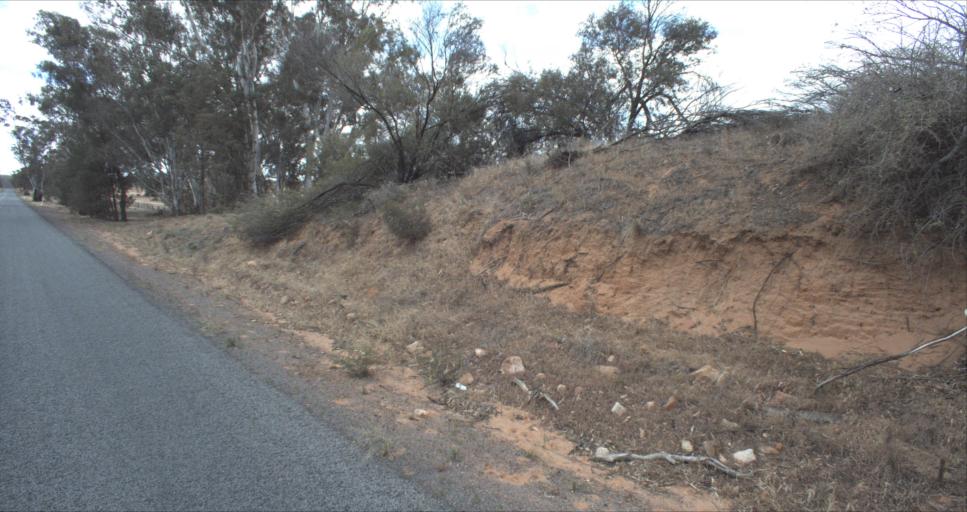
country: AU
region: New South Wales
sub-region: Leeton
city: Leeton
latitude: -34.6556
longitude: 146.3503
